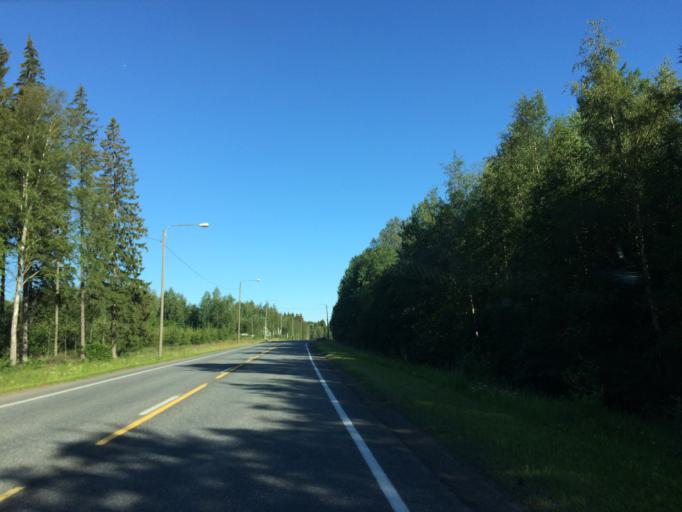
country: FI
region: Haeme
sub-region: Haemeenlinna
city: Haemeenlinna
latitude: 60.9544
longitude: 24.4957
